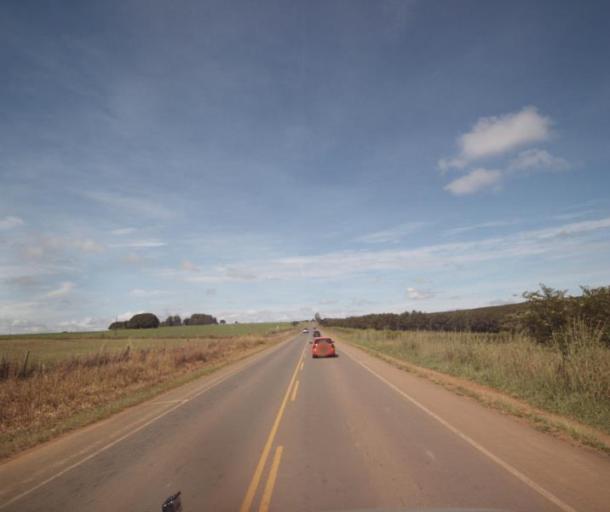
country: BR
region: Goias
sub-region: Anapolis
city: Anapolis
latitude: -16.1856
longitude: -48.9037
